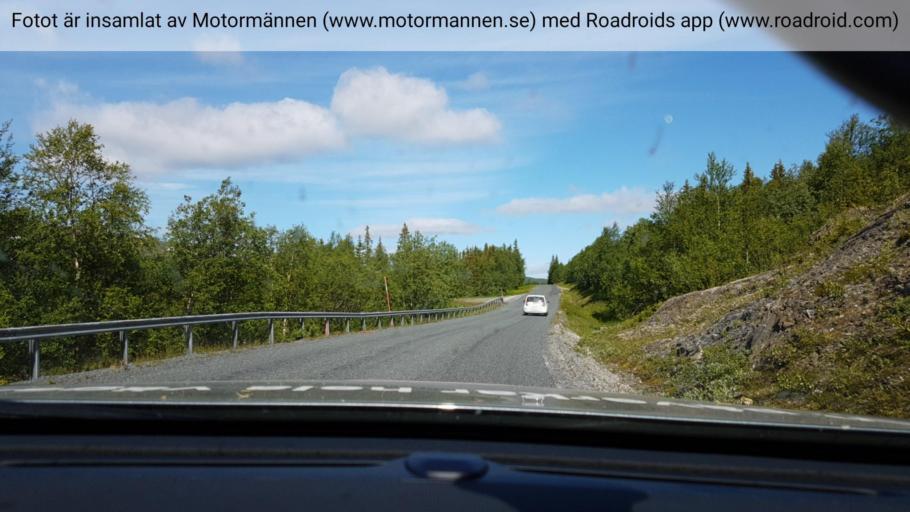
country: SE
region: Vaesterbotten
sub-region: Vilhelmina Kommun
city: Sjoberg
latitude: 65.2806
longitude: 15.3032
